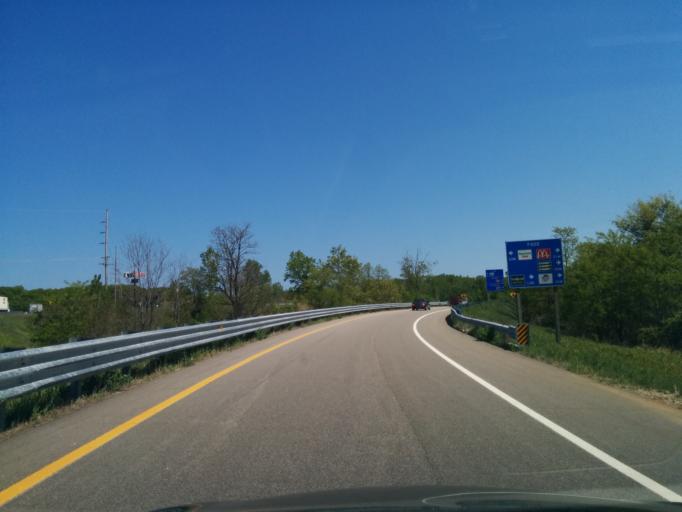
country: US
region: Michigan
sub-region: Berrien County
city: Bridgman
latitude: 41.9278
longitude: -86.5703
